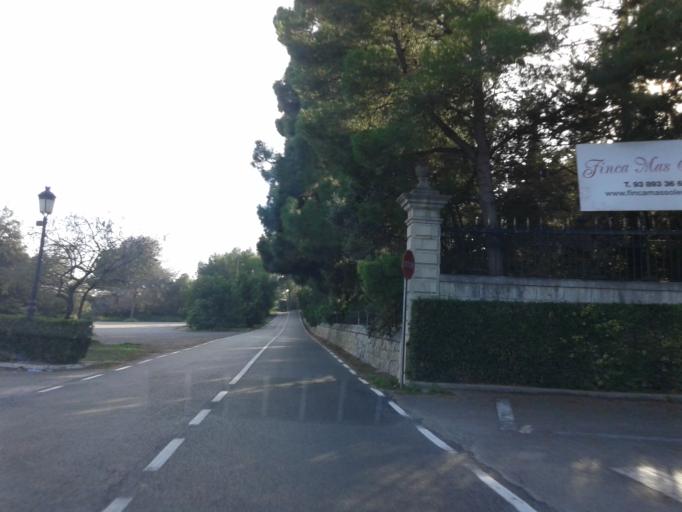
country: ES
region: Catalonia
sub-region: Provincia de Barcelona
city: Vilanova i la Geltru
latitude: 41.2449
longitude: 1.7449
